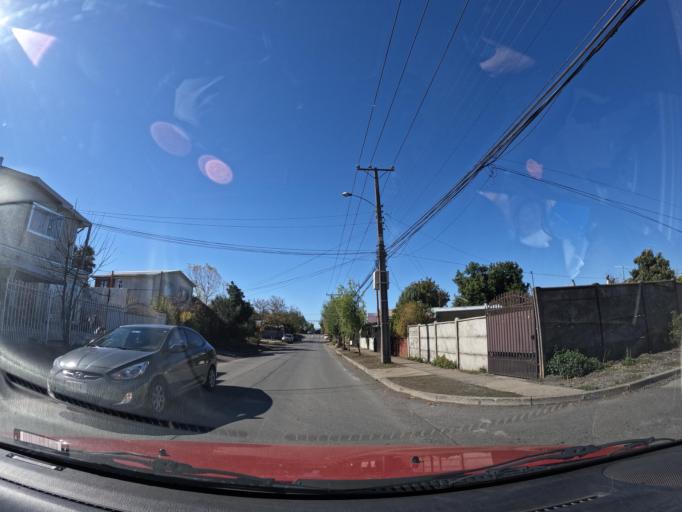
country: CL
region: Biobio
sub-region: Provincia de Nuble
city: Chillan
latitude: -36.6273
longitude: -72.1044
